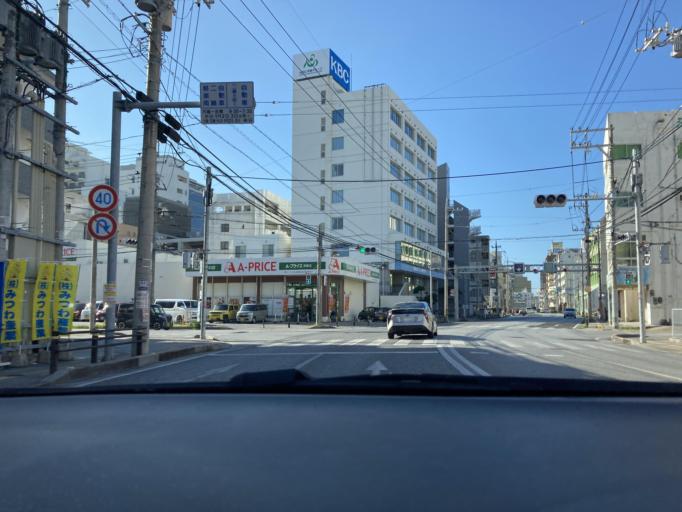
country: JP
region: Okinawa
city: Naha-shi
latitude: 26.2052
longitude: 127.6810
